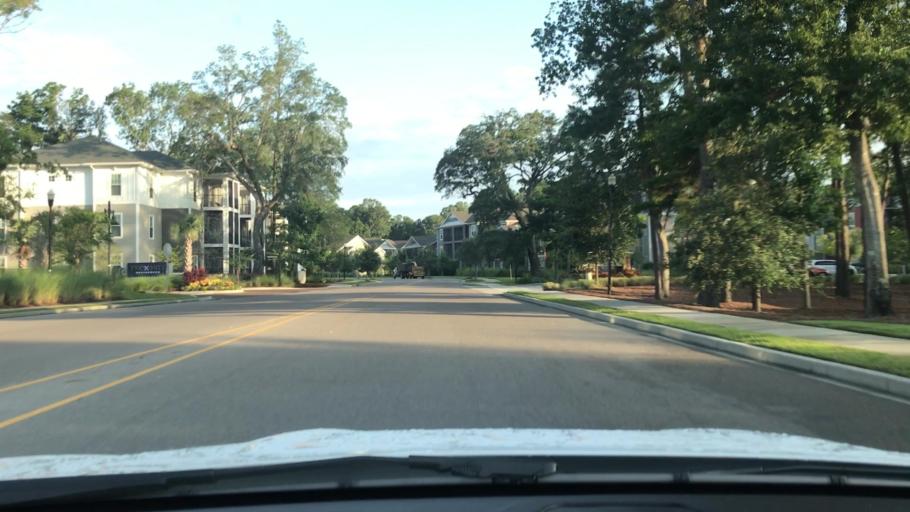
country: US
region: South Carolina
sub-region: Charleston County
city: Shell Point
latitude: 32.8229
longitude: -80.0885
